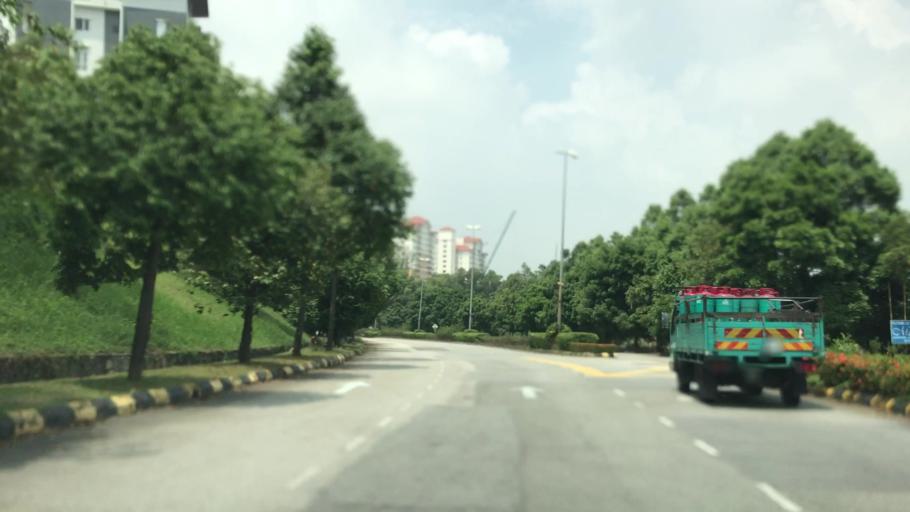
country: MY
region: Selangor
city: Subang Jaya
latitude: 3.0061
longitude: 101.6268
